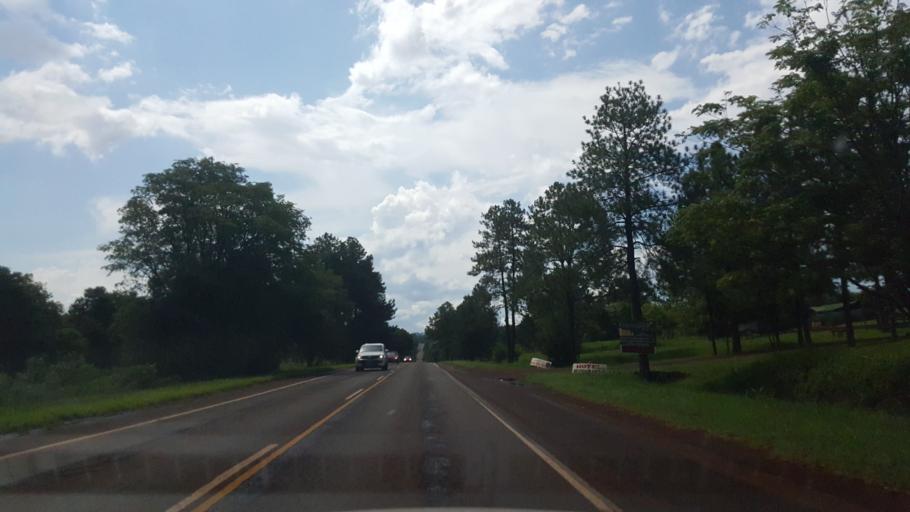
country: AR
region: Misiones
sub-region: Departamento de Eldorado
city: Eldorado
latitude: -26.3078
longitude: -54.6163
